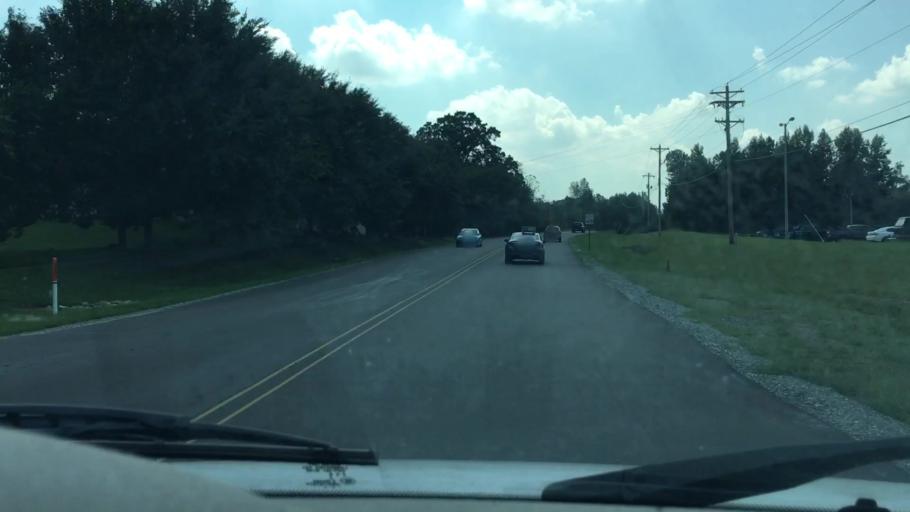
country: US
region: North Carolina
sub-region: Mecklenburg County
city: Huntersville
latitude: 35.3964
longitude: -80.8518
